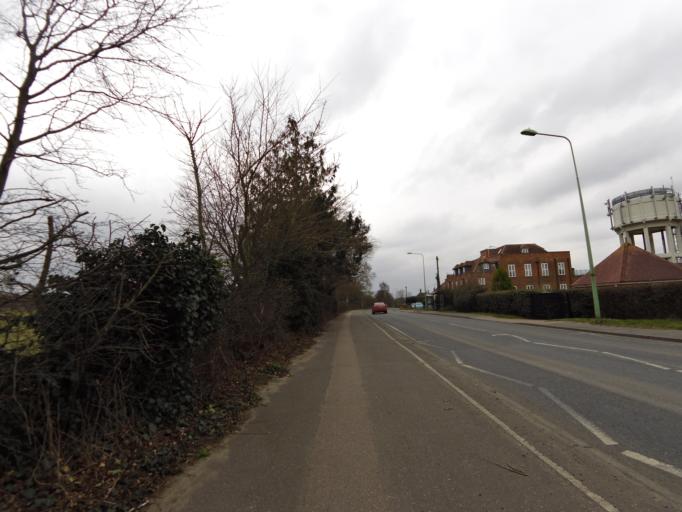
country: GB
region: England
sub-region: Suffolk
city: Halesworth
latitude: 52.3505
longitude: 1.5087
